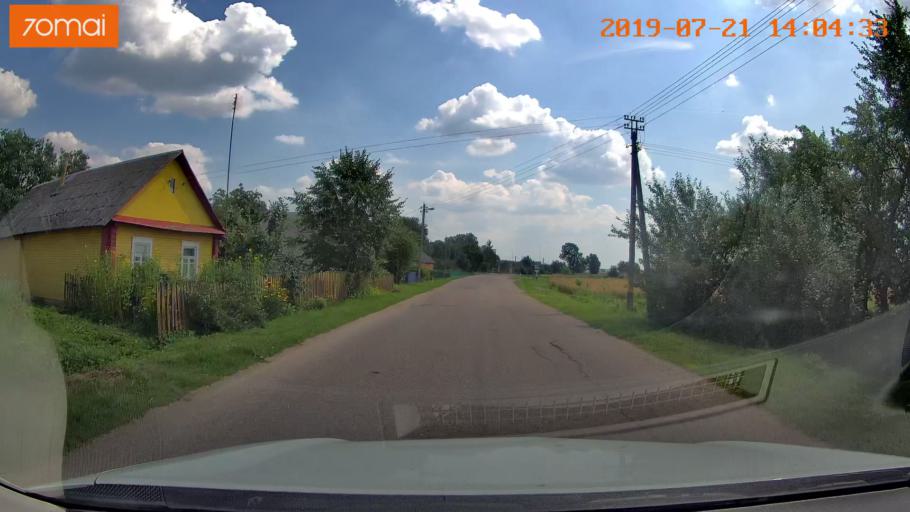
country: BY
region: Grodnenskaya
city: Lyubcha
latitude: 53.7195
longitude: 26.1002
